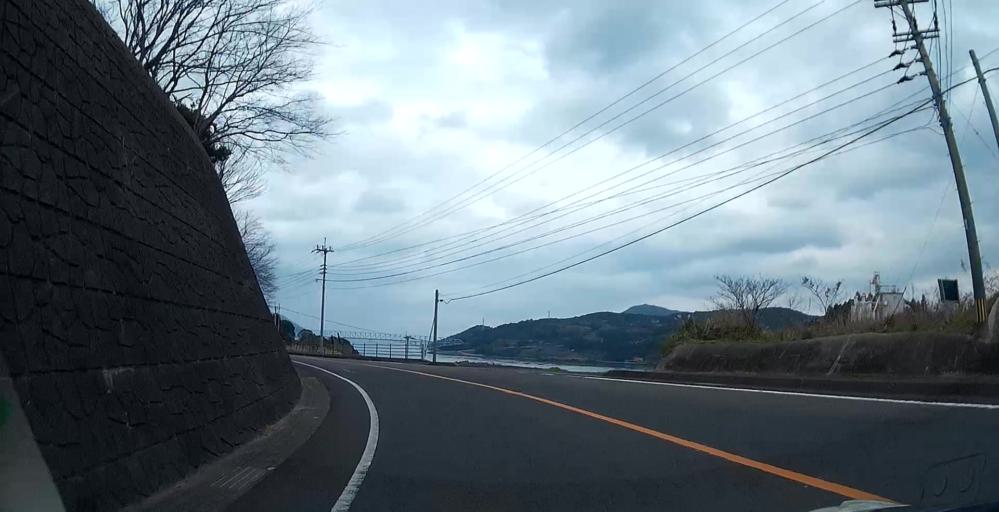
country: JP
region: Kagoshima
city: Akune
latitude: 32.0961
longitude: 130.1651
